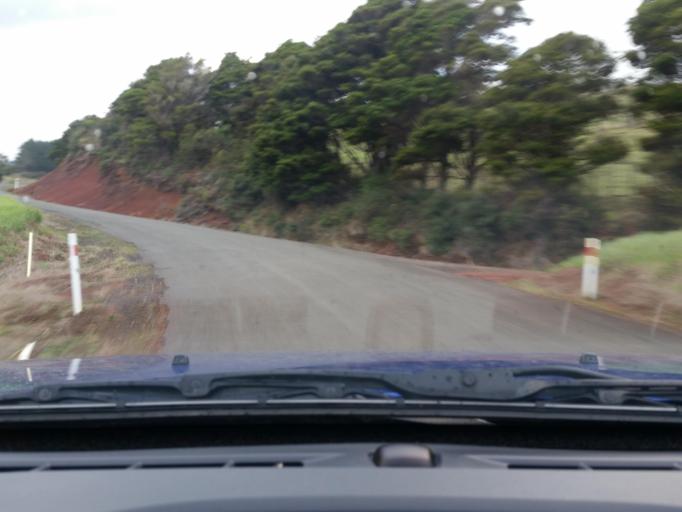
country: NZ
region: Northland
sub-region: Kaipara District
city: Dargaville
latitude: -35.7654
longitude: 173.6084
